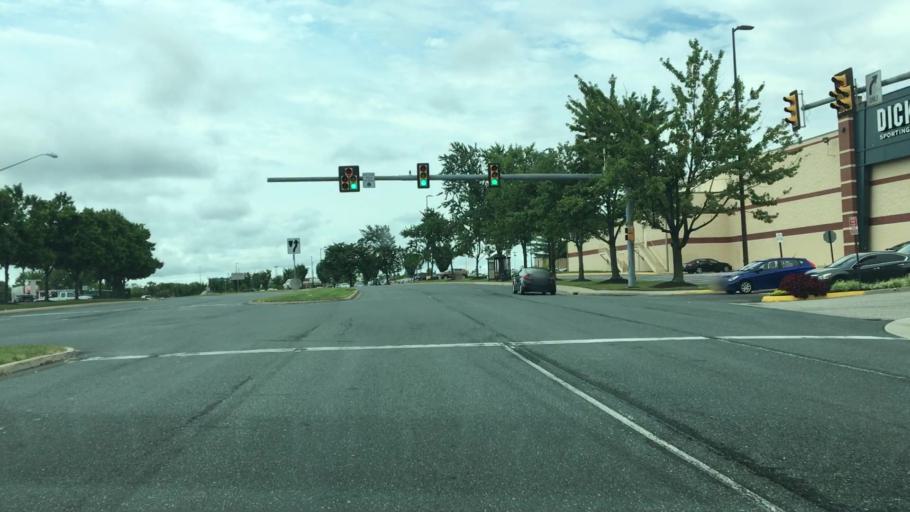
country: US
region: Virginia
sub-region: Prince William County
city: Potomac Mills
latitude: 38.6504
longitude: -77.2950
